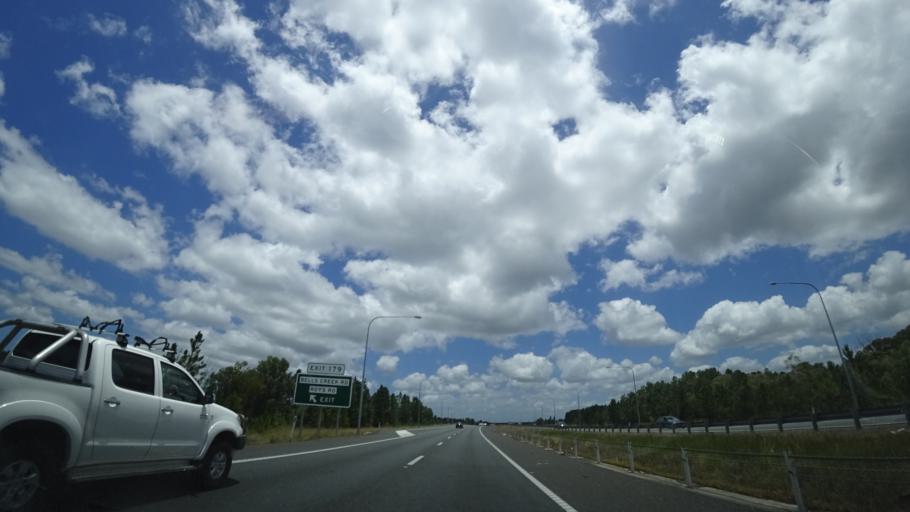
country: AU
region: Queensland
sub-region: Sunshine Coast
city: Little Mountain
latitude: -26.8451
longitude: 153.0305
